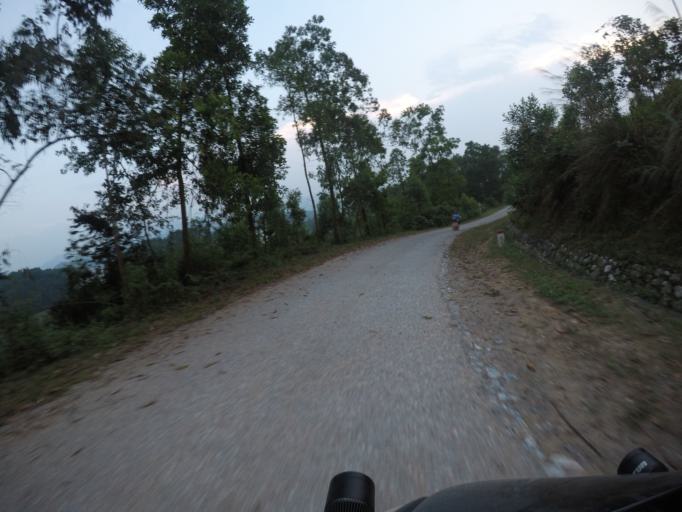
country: VN
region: Thai Nguyen
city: Chua Hang
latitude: 21.5819
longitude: 105.7136
